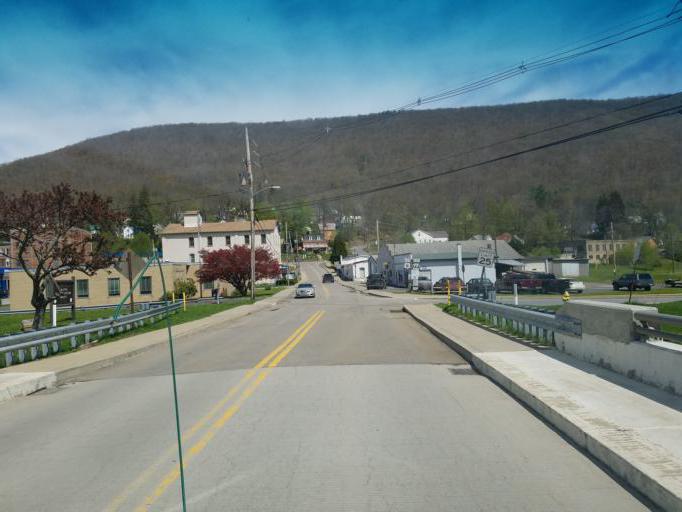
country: US
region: Pennsylvania
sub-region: Potter County
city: Galeton
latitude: 41.7339
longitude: -77.6421
